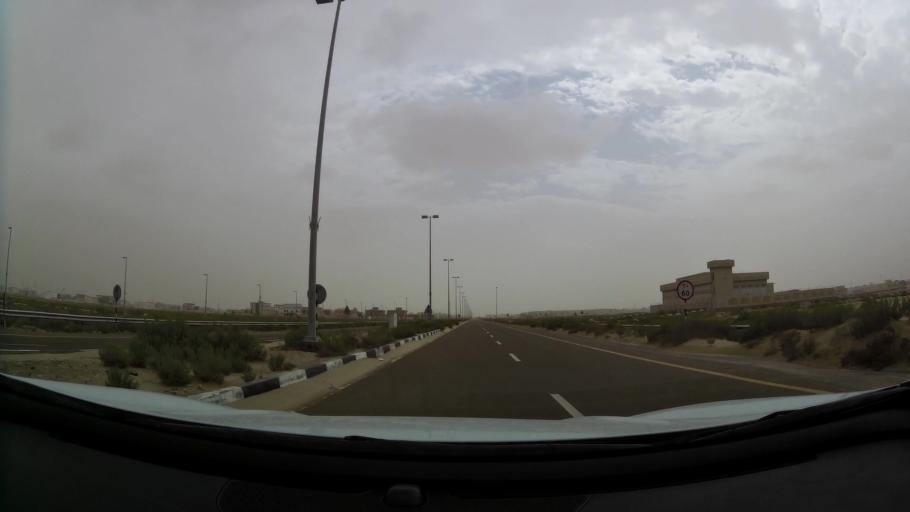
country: AE
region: Abu Dhabi
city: Abu Dhabi
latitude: 24.3703
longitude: 54.6865
